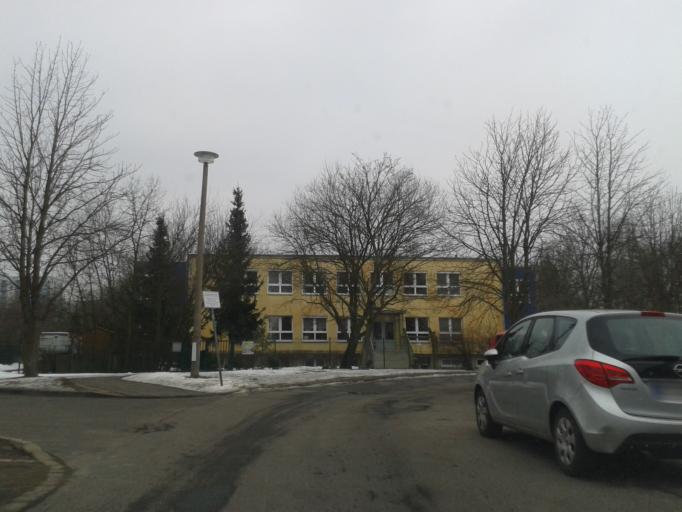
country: DE
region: Saxony
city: Dresden
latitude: 51.0218
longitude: 13.7365
